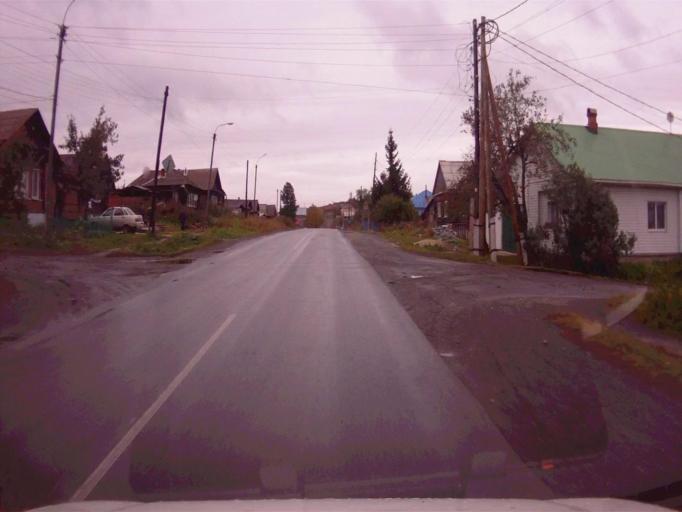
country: RU
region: Chelyabinsk
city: Verkhniy Ufaley
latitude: 56.0554
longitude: 60.2043
